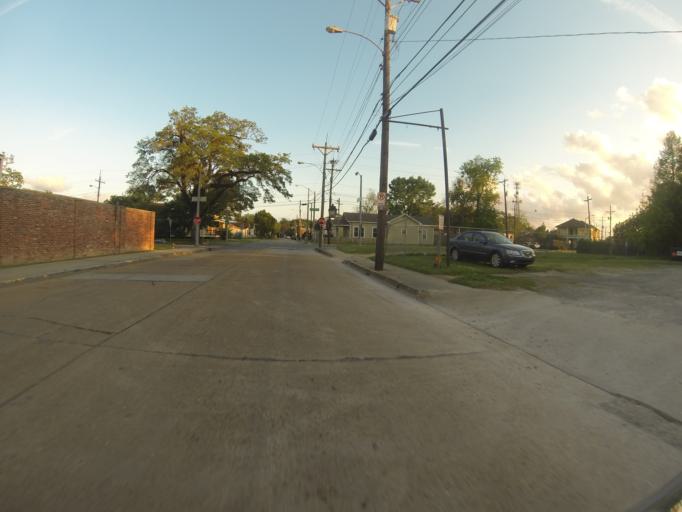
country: US
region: Louisiana
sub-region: Lafayette Parish
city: Lafayette
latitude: 30.2262
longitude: -92.0151
